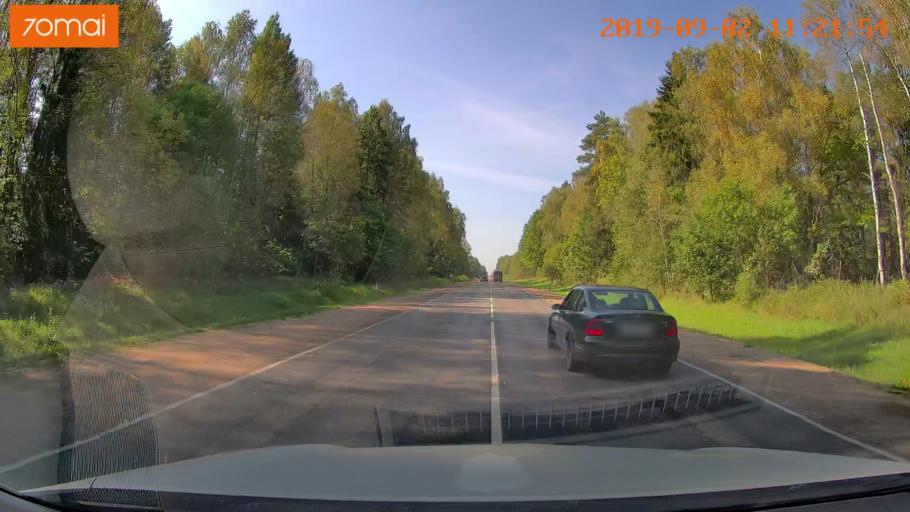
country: RU
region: Smolensk
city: Roslavl'
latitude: 54.0307
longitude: 33.0255
